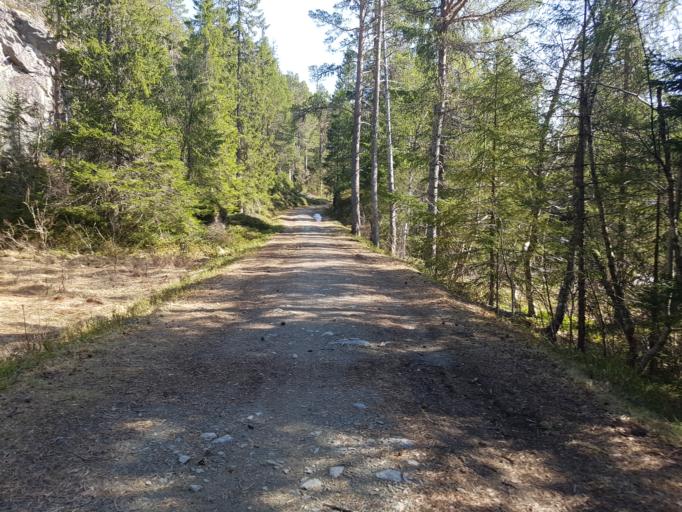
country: NO
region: Sor-Trondelag
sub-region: Trondheim
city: Trondheim
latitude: 63.4338
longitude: 10.2919
